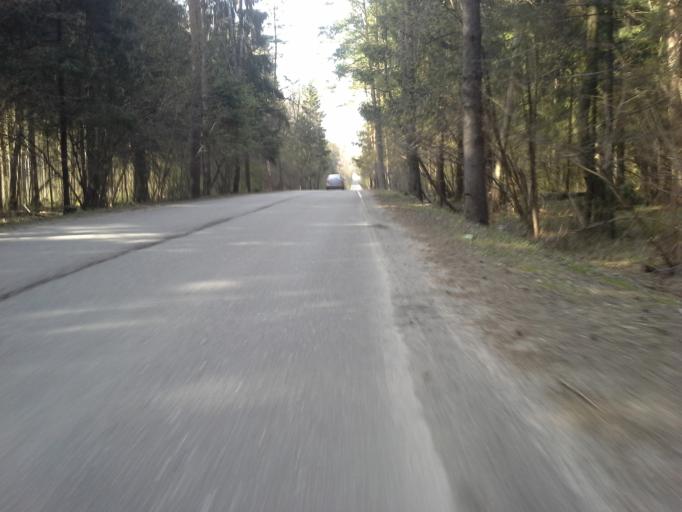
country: RU
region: Moskovskaya
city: Dubrovitsy
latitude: 55.4345
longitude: 37.3989
